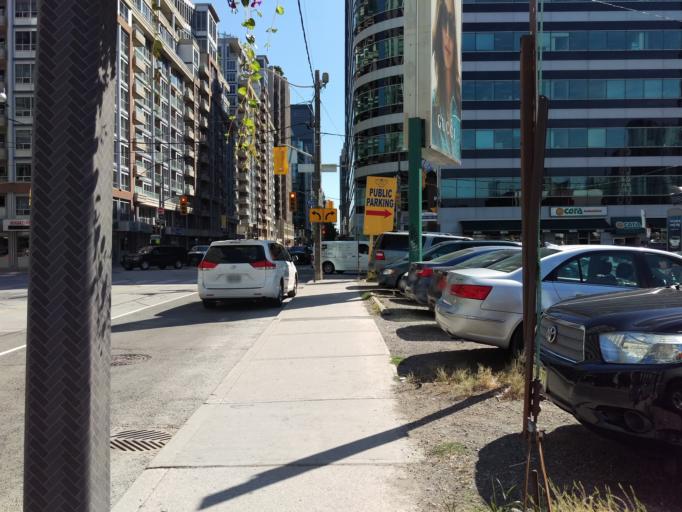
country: CA
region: Ontario
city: Toronto
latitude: 43.6446
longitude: -79.3922
